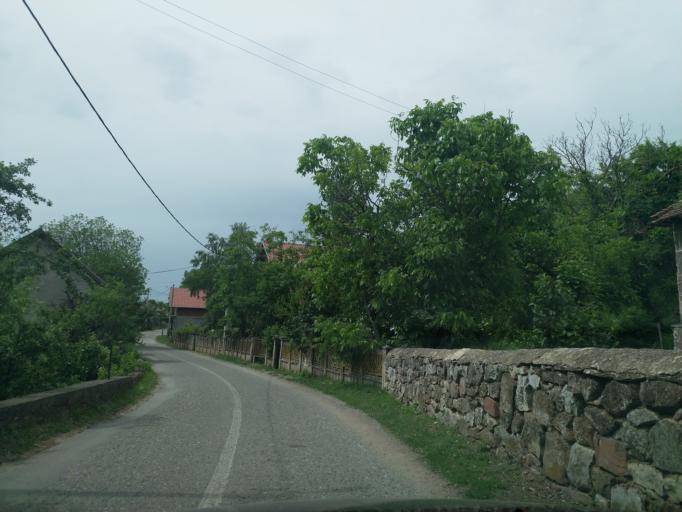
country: RS
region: Central Serbia
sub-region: Pomoravski Okrug
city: Paracin
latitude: 43.8619
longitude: 21.5885
